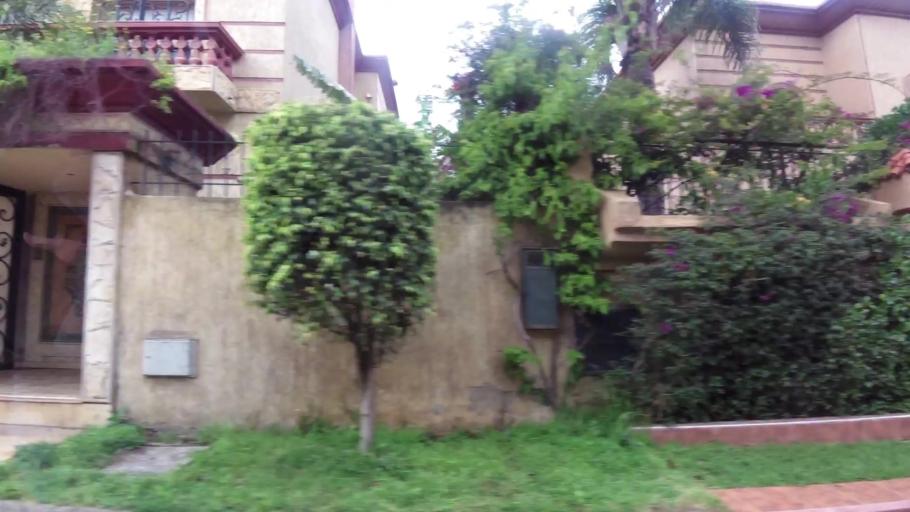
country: MA
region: Grand Casablanca
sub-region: Nouaceur
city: Bouskoura
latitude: 33.5169
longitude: -7.6392
